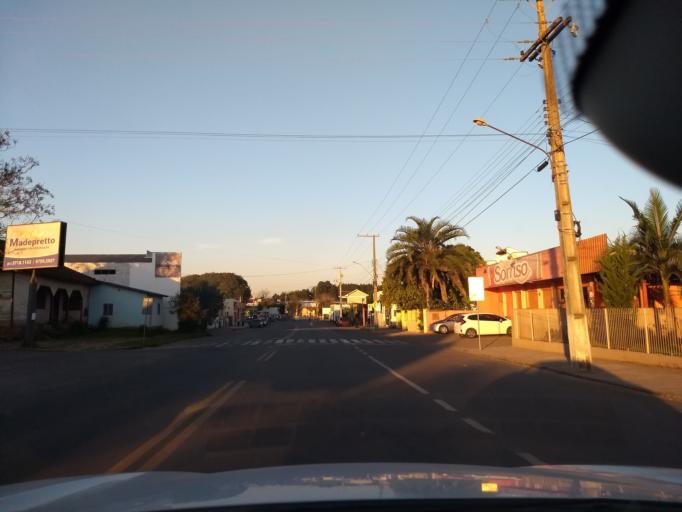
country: BR
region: Rio Grande do Sul
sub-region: Santa Cruz Do Sul
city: Santa Cruz do Sul
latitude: -29.7195
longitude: -52.5145
